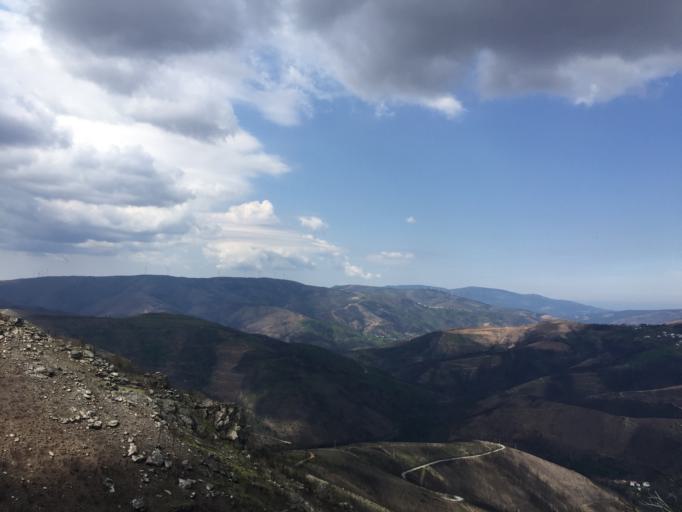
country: PT
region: Coimbra
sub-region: Pampilhosa da Serra
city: Pampilhosa da Serra
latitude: 40.1612
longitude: -7.9303
